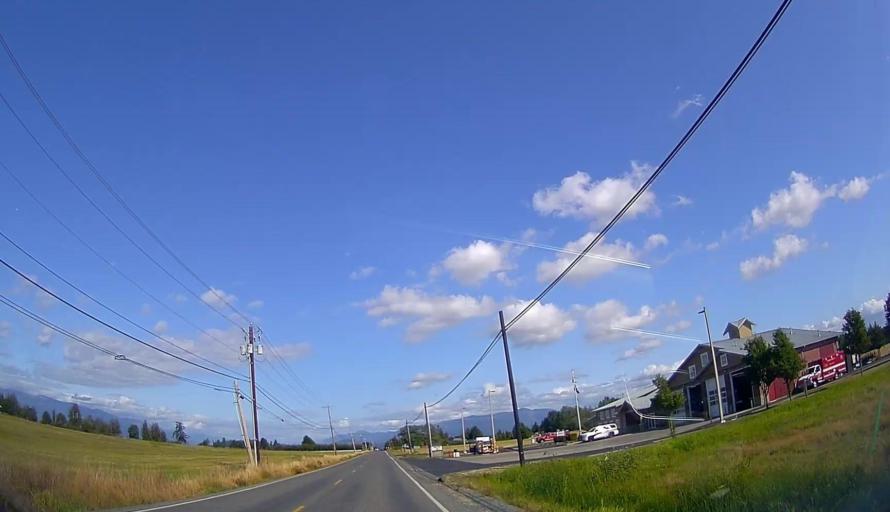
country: US
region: Washington
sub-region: Skagit County
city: Burlington
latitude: 48.4722
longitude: -122.3964
